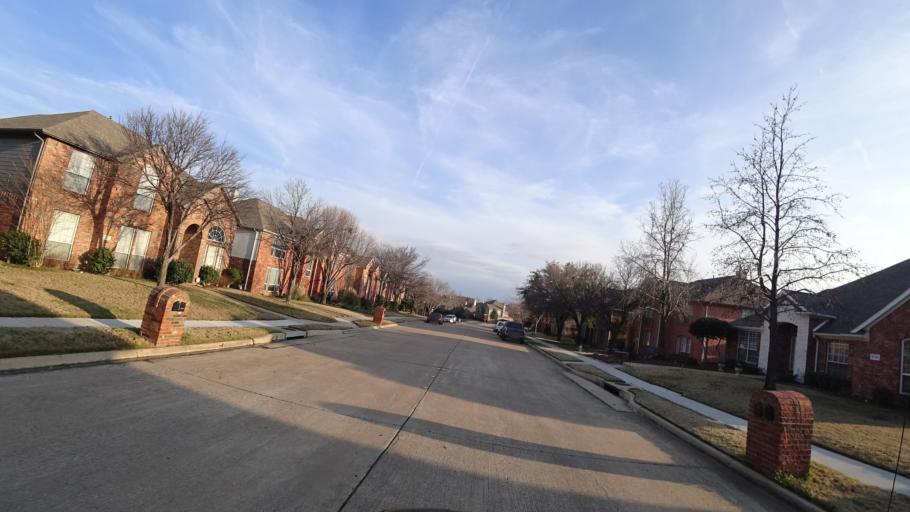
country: US
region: Texas
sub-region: Dallas County
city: Coppell
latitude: 32.9950
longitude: -96.9859
